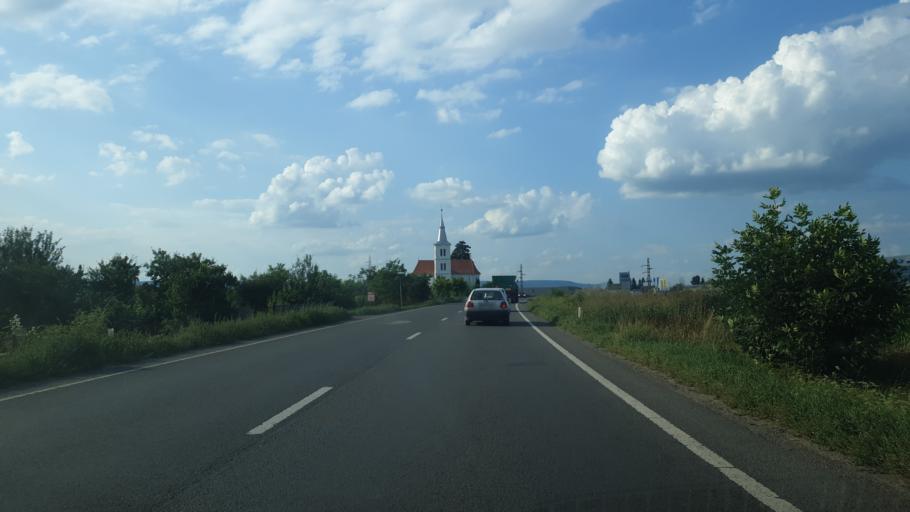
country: RO
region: Covasna
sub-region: Municipiul Sfantu Gheorghe
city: Sfantu-Gheorghe
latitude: 45.8395
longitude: 25.8035
